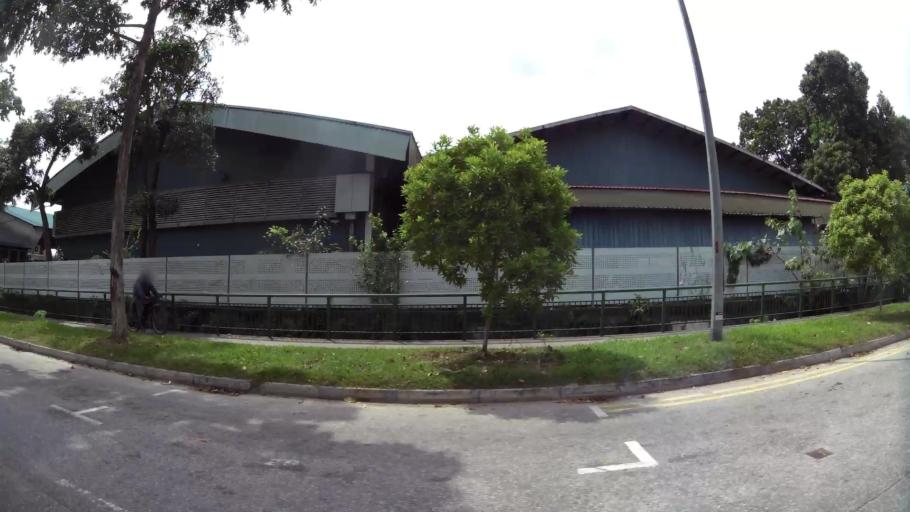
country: MY
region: Johor
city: Johor Bahru
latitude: 1.4233
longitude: 103.7500
